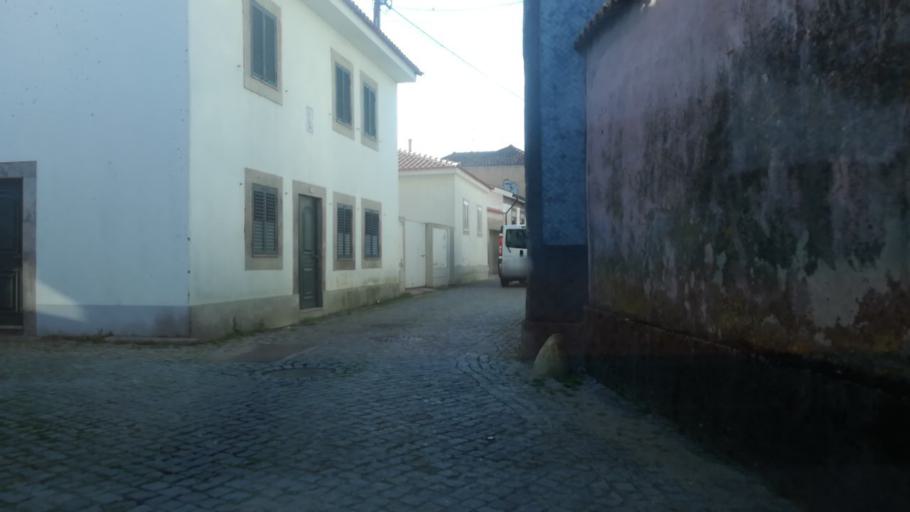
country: PT
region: Porto
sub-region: Matosinhos
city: Santa Cruz do Bispo
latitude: 41.2505
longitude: -8.6720
